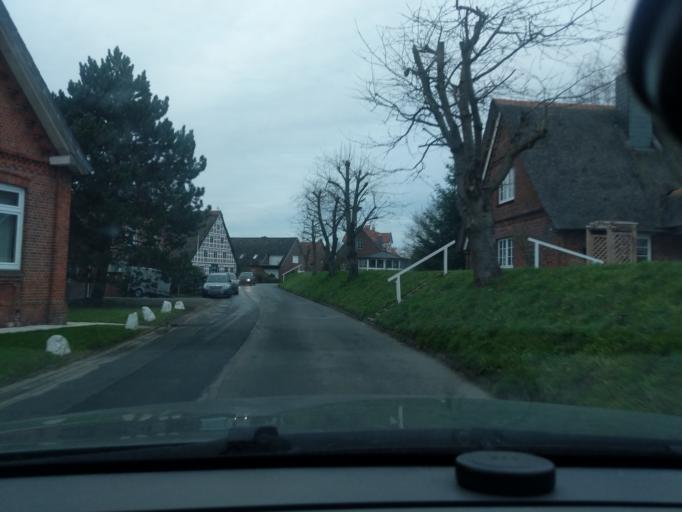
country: DE
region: Lower Saxony
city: Mittelnkirchen
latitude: 53.5333
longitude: 9.6128
